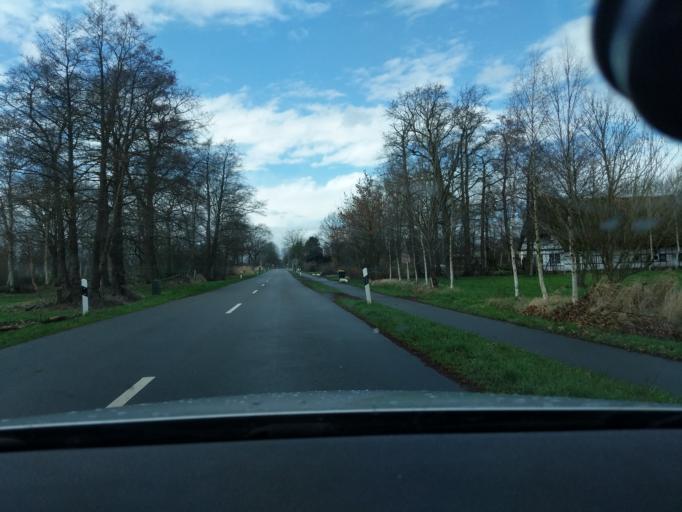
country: DE
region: Lower Saxony
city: Engelschoff
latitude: 53.6765
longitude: 9.3597
